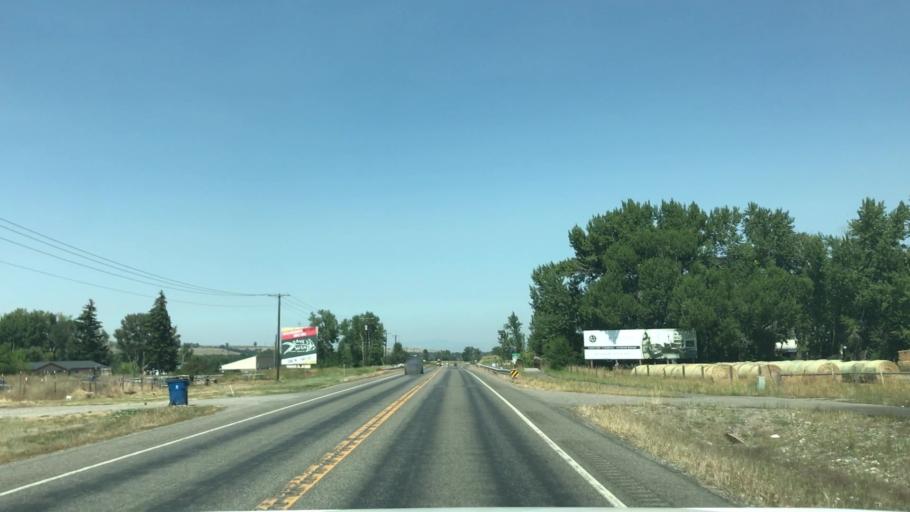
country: US
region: Montana
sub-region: Gallatin County
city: Four Corners
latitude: 45.6102
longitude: -111.1960
